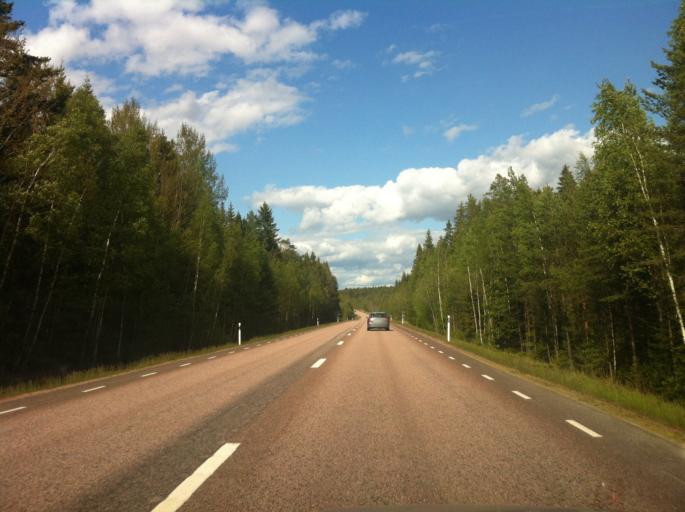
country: SE
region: Vaermland
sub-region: Kristinehamns Kommun
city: Kristinehamn
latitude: 59.3410
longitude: 14.1277
